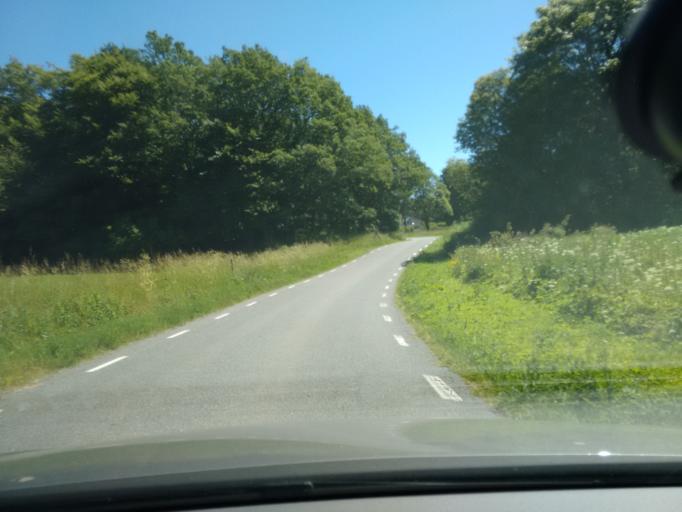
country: SE
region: Skane
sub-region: Kristianstads Kommun
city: Degeberga
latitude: 55.7783
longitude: 14.0324
